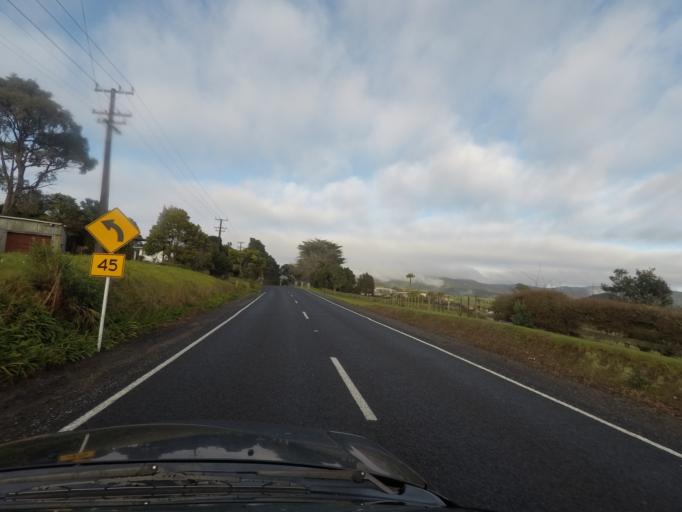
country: NZ
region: Auckland
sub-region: Auckland
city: Waitakere
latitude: -36.9065
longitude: 174.6089
